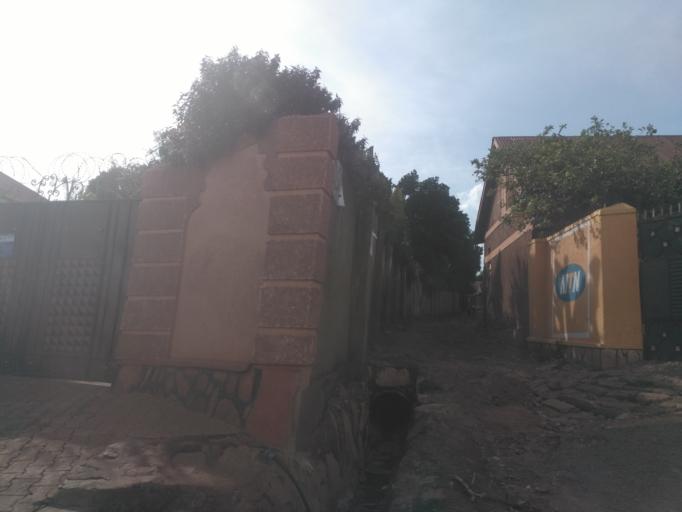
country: UG
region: Central Region
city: Kampala Central Division
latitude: 0.3562
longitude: 32.5695
